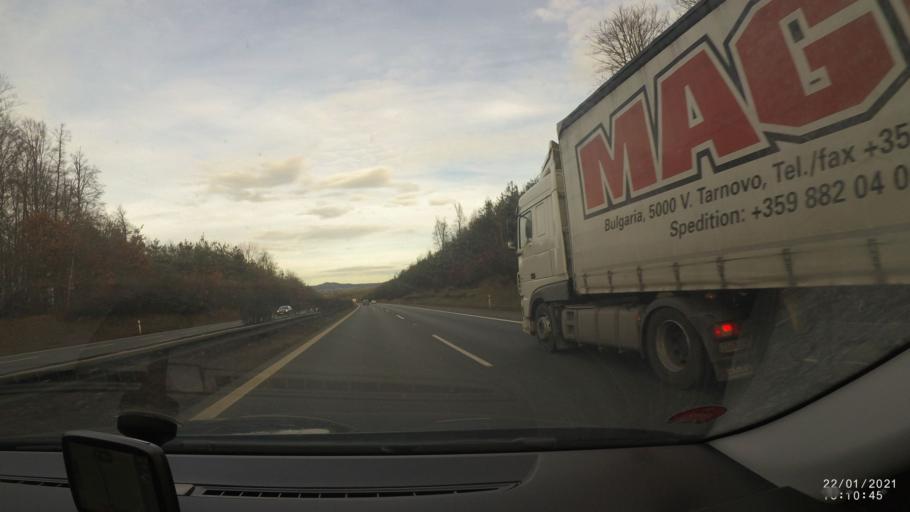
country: CZ
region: Plzensky
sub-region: Okres Rokycany
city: Rokycany
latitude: 49.7409
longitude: 13.5384
